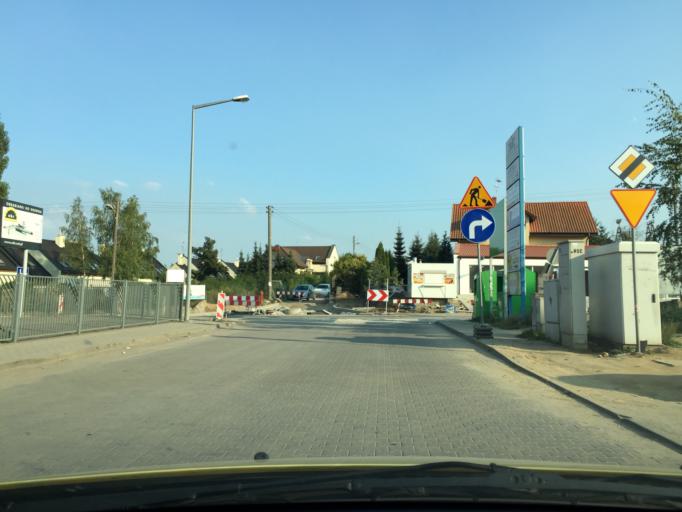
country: PL
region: Greater Poland Voivodeship
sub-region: Powiat poznanski
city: Plewiska
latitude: 52.3717
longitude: 16.8162
